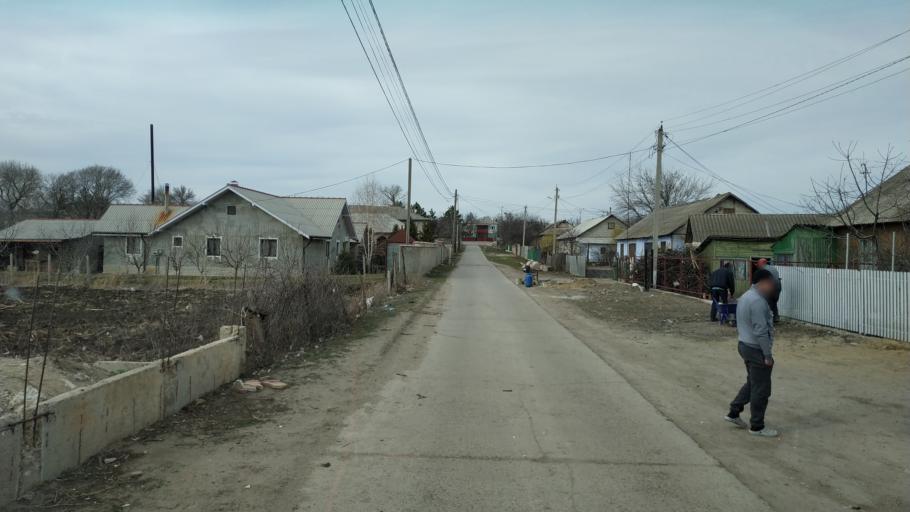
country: MD
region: Hincesti
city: Dancu
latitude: 46.8572
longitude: 28.2514
